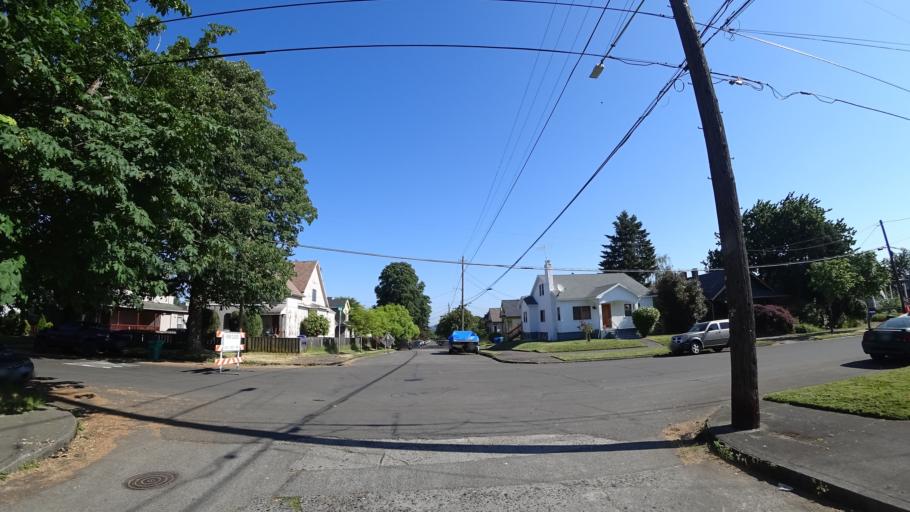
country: US
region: Oregon
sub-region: Multnomah County
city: Portland
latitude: 45.5717
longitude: -122.6634
